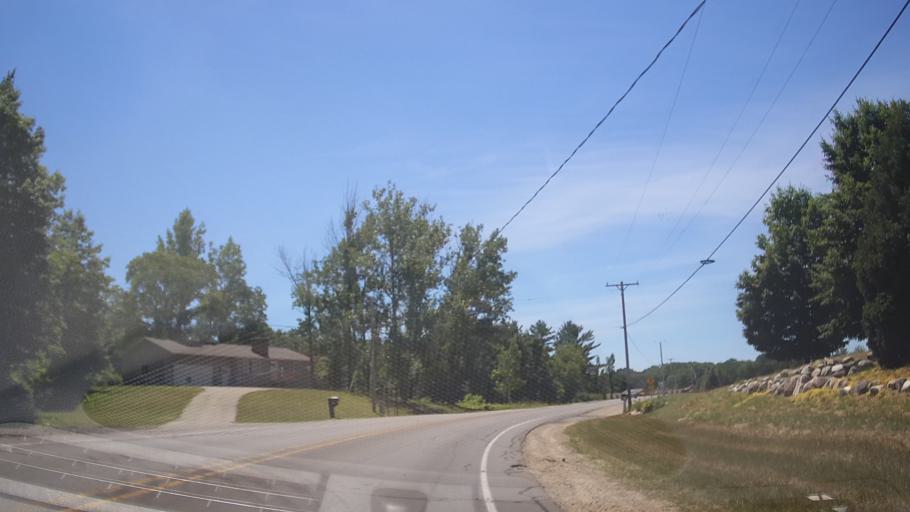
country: US
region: Michigan
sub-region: Grand Traverse County
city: Traverse City
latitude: 44.7142
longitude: -85.6865
